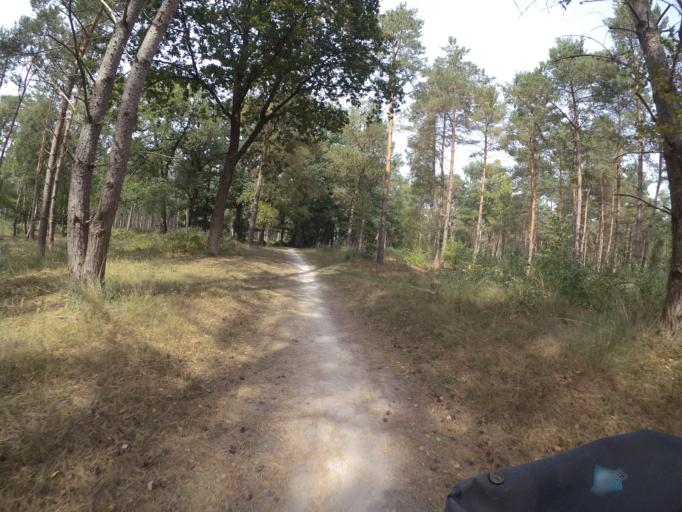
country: NL
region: Drenthe
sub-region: Gemeente Westerveld
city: Havelte
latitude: 52.8116
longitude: 6.2642
